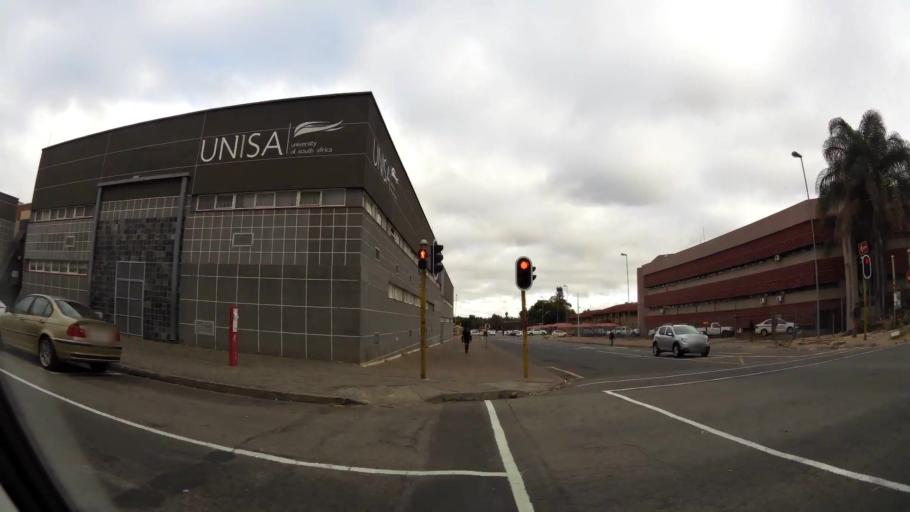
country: ZA
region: Limpopo
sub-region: Capricorn District Municipality
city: Polokwane
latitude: -23.9159
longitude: 29.4544
